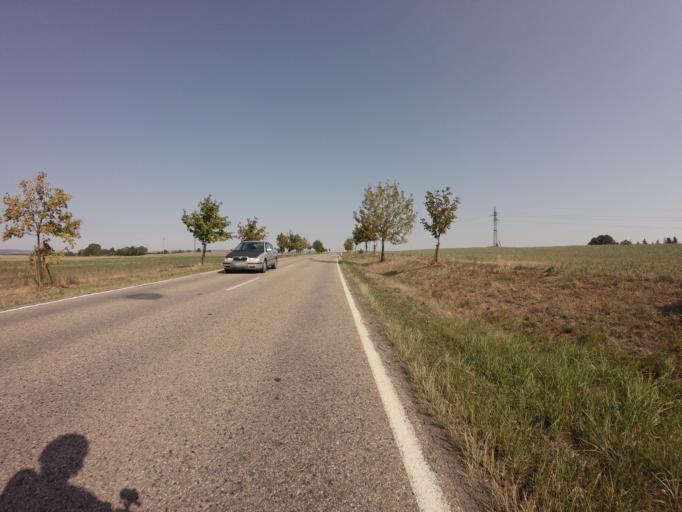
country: CZ
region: Central Bohemia
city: Porici nad Sazavou
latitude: 49.8056
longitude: 14.6505
